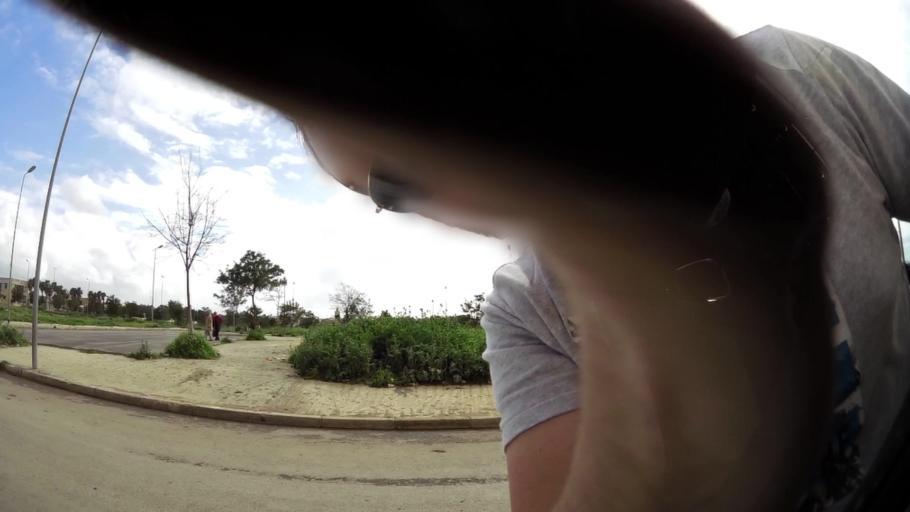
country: MA
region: Grand Casablanca
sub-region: Mohammedia
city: Mohammedia
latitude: 33.6795
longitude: -7.3787
